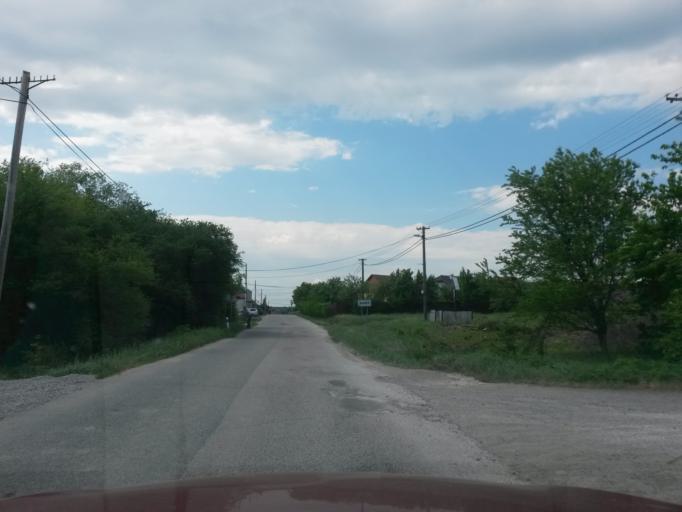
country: SK
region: Kosicky
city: Moldava nad Bodvou
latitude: 48.6970
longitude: 21.0121
